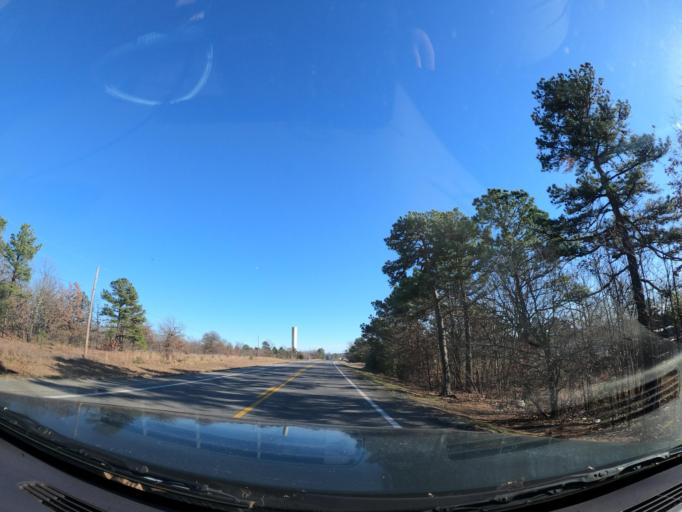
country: US
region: Oklahoma
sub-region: Pittsburg County
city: Longtown
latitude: 35.2304
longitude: -95.4541
